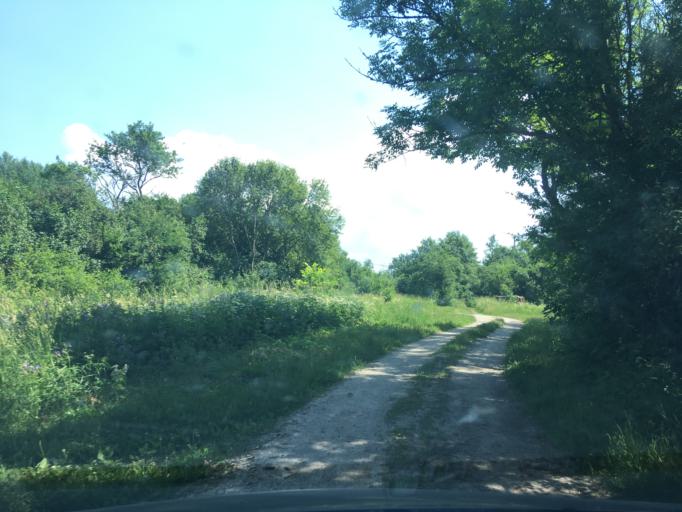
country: EE
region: Raplamaa
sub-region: Maerjamaa vald
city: Marjamaa
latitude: 58.7349
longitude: 24.1608
